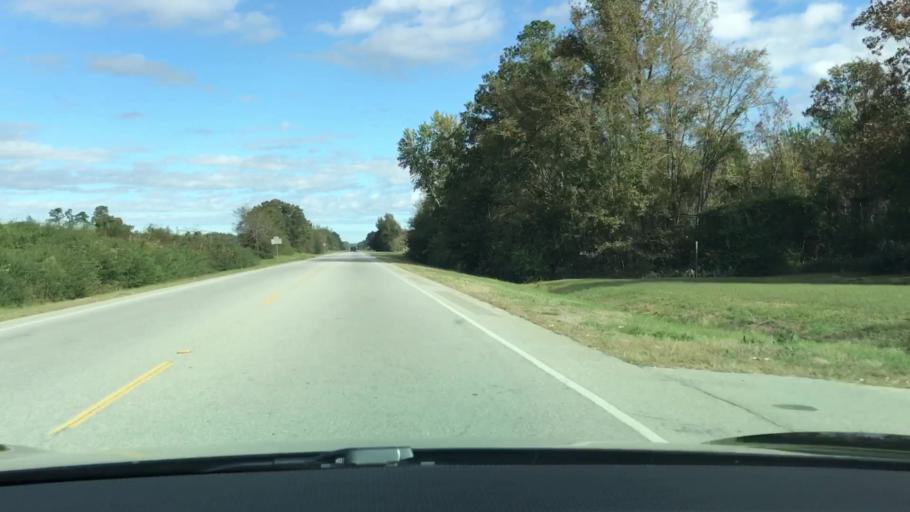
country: US
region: Georgia
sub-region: Jefferson County
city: Wadley
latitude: 32.9247
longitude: -82.3974
